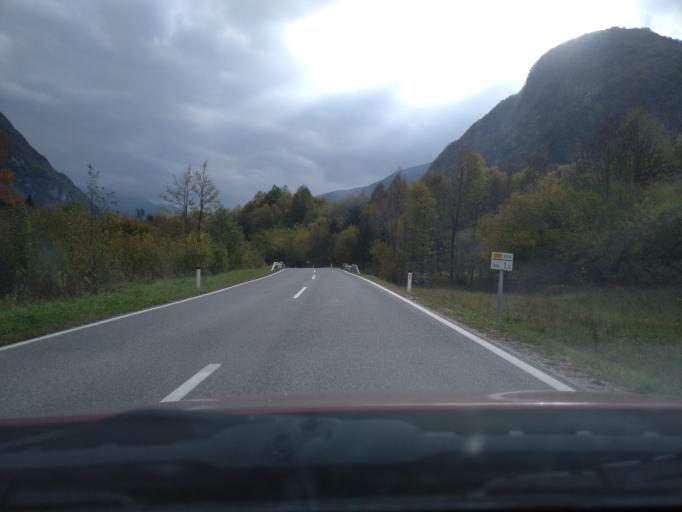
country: SI
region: Bovec
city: Bovec
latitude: 46.2982
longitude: 13.4870
